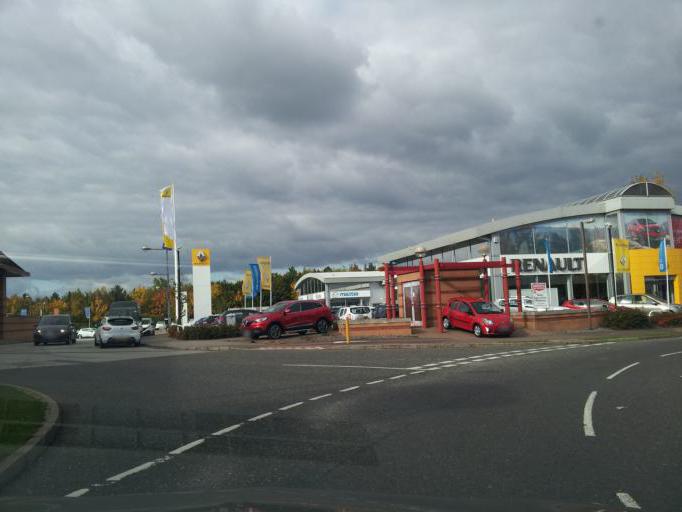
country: GB
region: England
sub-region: Milton Keynes
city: Shenley Church End
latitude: 52.0057
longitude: -0.7932
